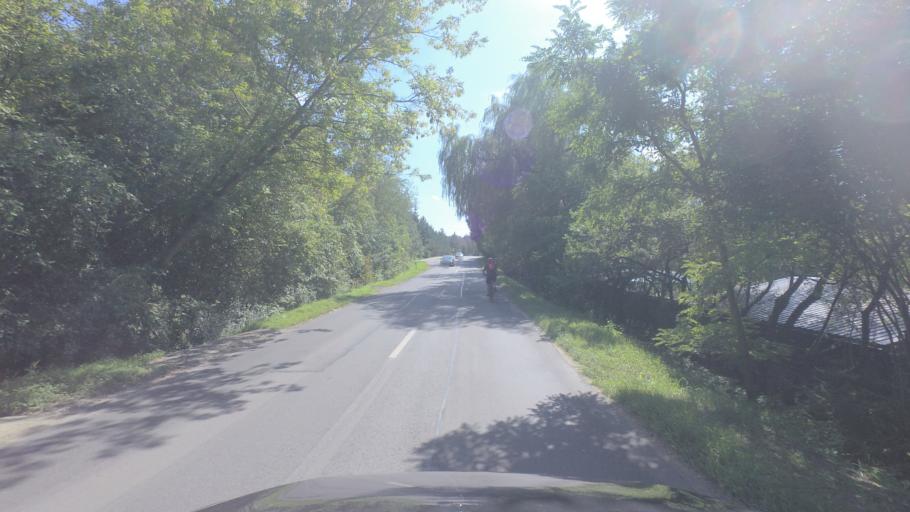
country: LT
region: Vilnius County
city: Rasos
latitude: 54.7929
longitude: 25.3509
